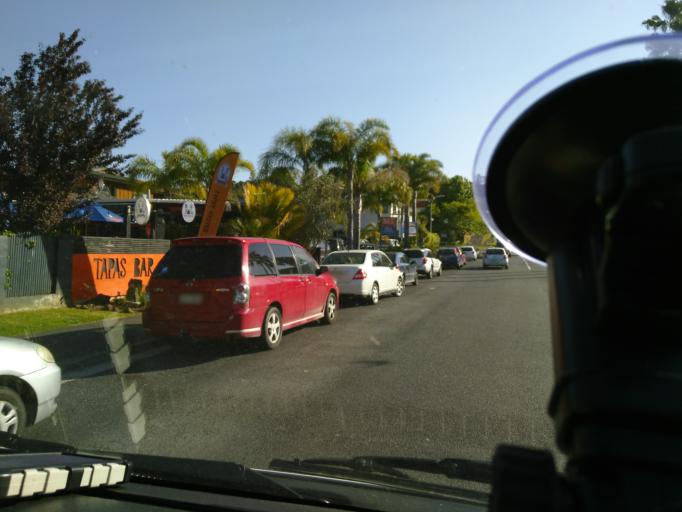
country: NZ
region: Northland
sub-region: Far North District
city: Paihia
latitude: -35.2856
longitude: 174.0947
